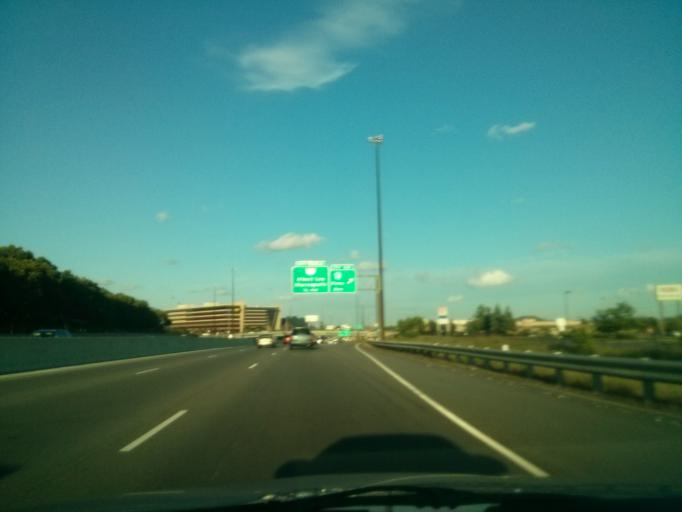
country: US
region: Minnesota
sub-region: Hennepin County
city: Bloomington
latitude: 44.8617
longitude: -93.3143
